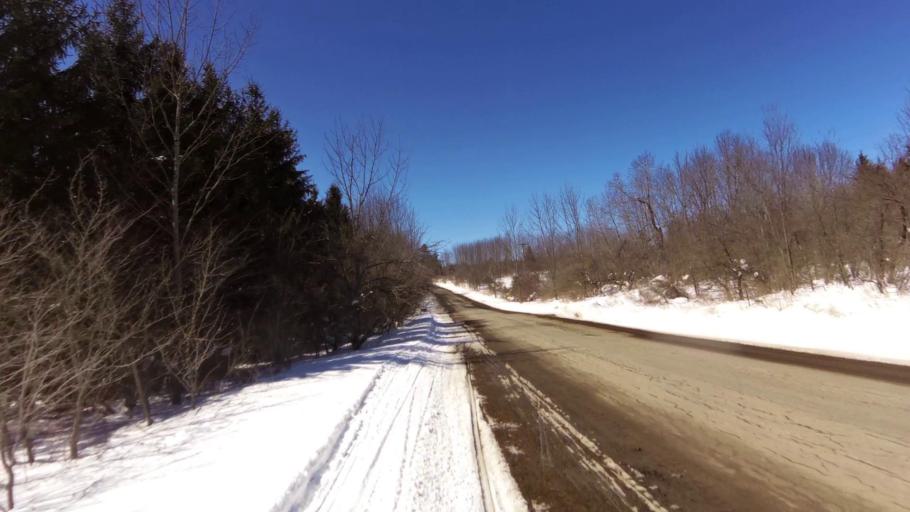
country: US
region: New York
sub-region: Allegany County
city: Houghton
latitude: 42.4129
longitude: -78.3036
